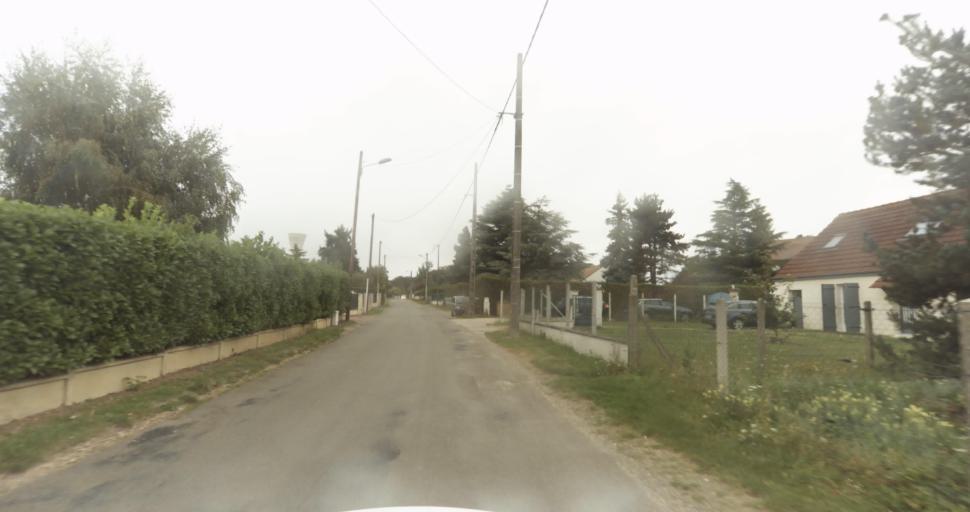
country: FR
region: Haute-Normandie
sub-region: Departement de l'Eure
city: Saint-Germain-sur-Avre
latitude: 48.7698
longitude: 1.2633
